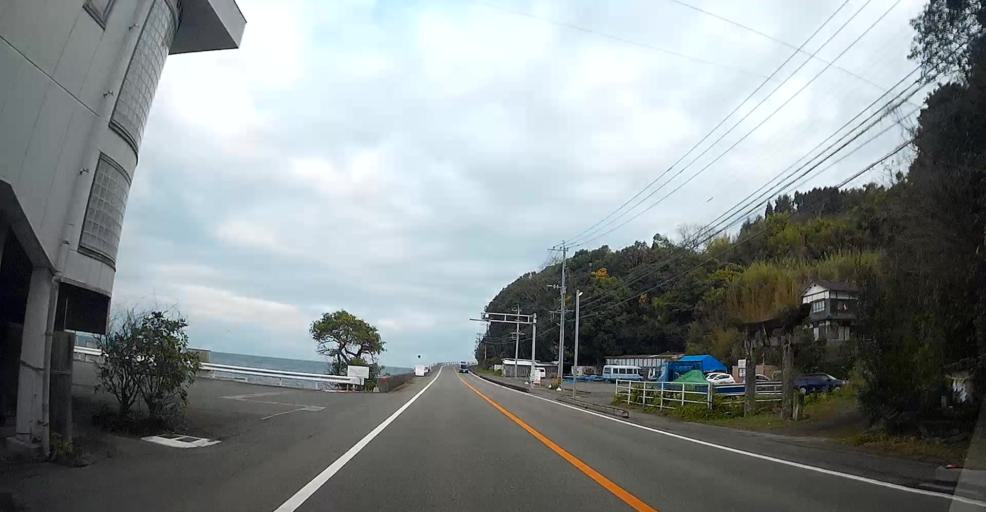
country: JP
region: Kumamoto
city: Hondo
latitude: 32.4554
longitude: 130.2145
